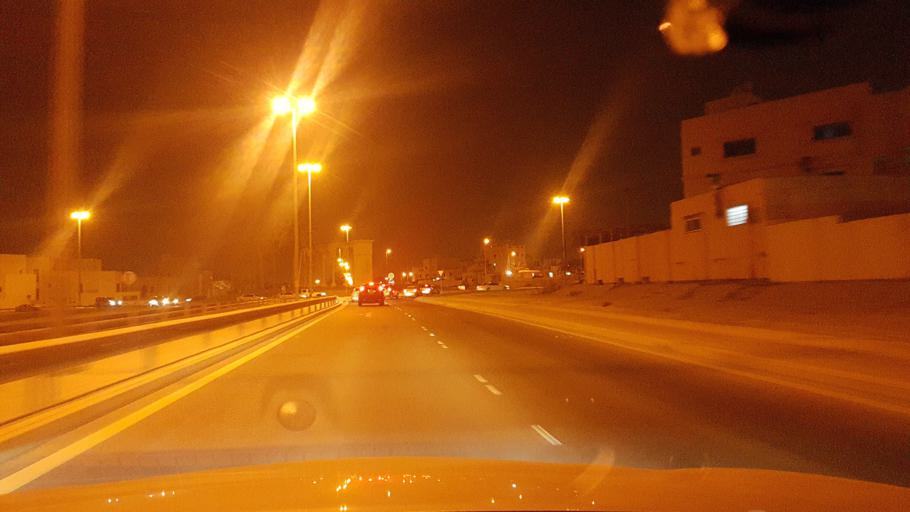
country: BH
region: Central Governorate
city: Madinat Hamad
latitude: 26.0957
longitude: 50.5008
